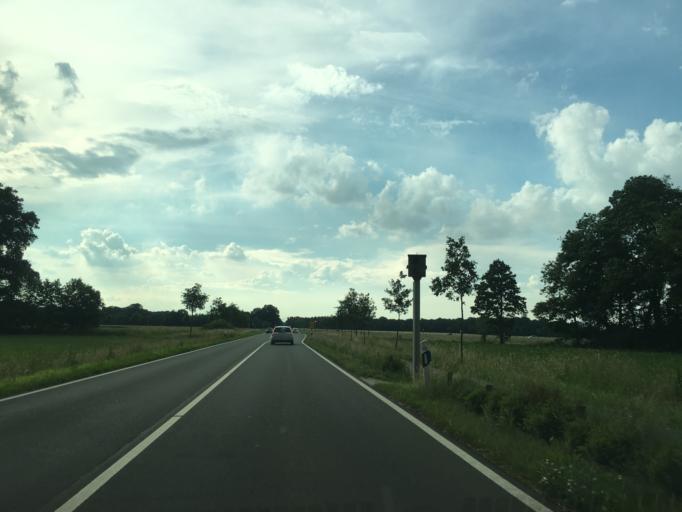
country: DE
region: North Rhine-Westphalia
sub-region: Regierungsbezirk Munster
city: Wettringen
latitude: 52.1783
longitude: 7.2778
